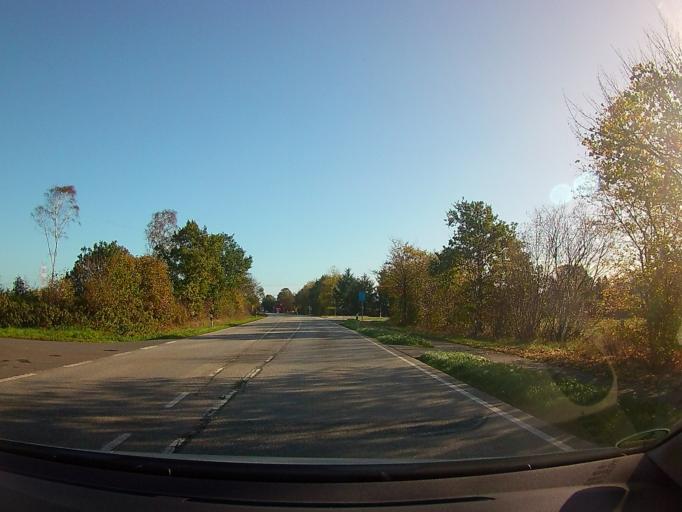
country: DE
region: Schleswig-Holstein
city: Ellingstedt
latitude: 54.5153
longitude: 9.4232
